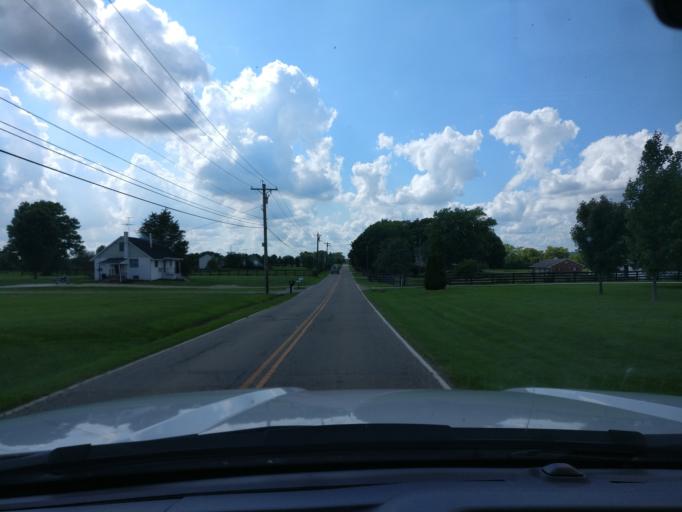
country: US
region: Ohio
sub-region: Warren County
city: Springboro
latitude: 39.5038
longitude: -84.2081
